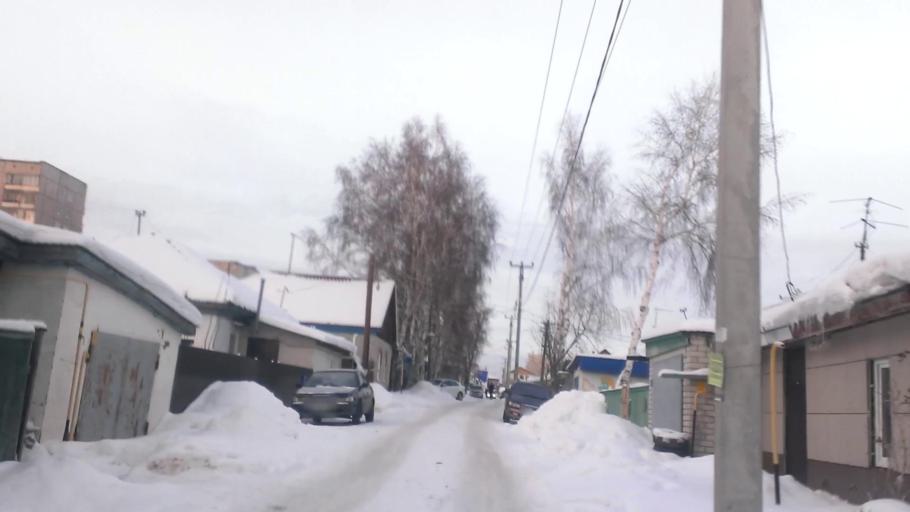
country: RU
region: Altai Krai
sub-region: Gorod Barnaulskiy
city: Barnaul
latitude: 53.3474
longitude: 83.6941
